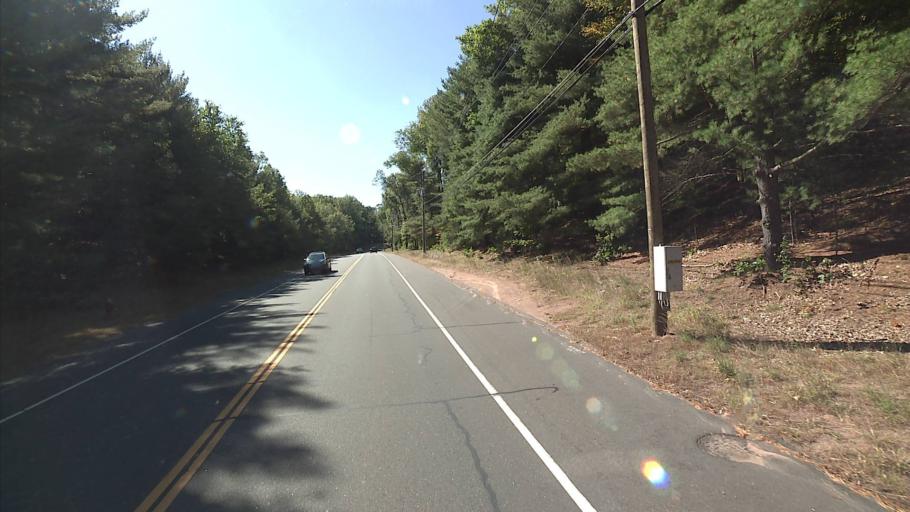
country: US
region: Connecticut
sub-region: Hartford County
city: Manchester
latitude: 41.7112
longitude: -72.5271
